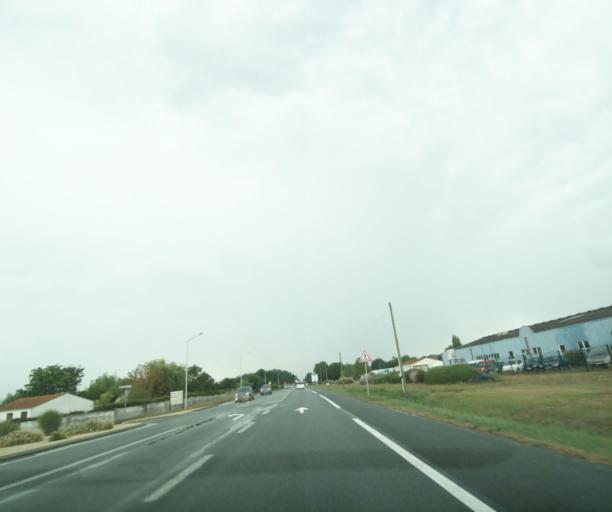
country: FR
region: Poitou-Charentes
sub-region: Departement de la Charente-Maritime
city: Tonnay-Charente
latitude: 45.9514
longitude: -0.8904
